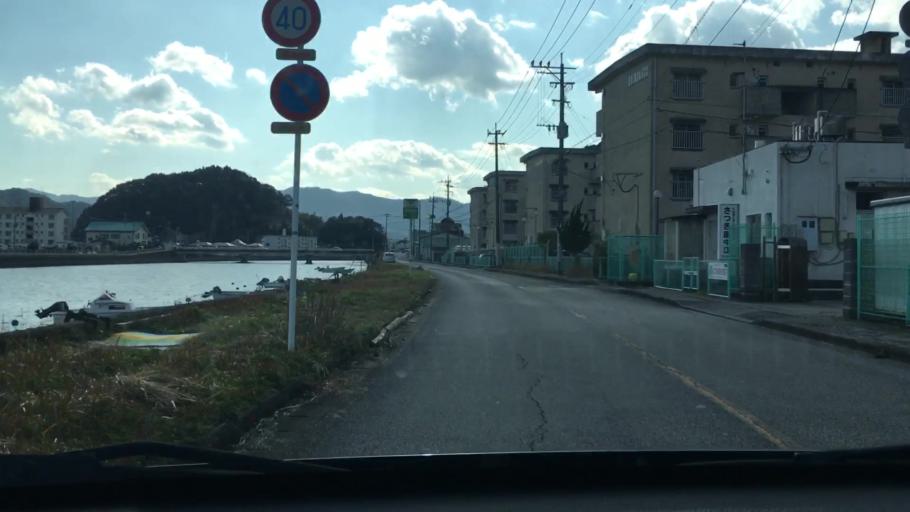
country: JP
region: Oita
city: Saiki
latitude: 32.9645
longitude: 131.9130
